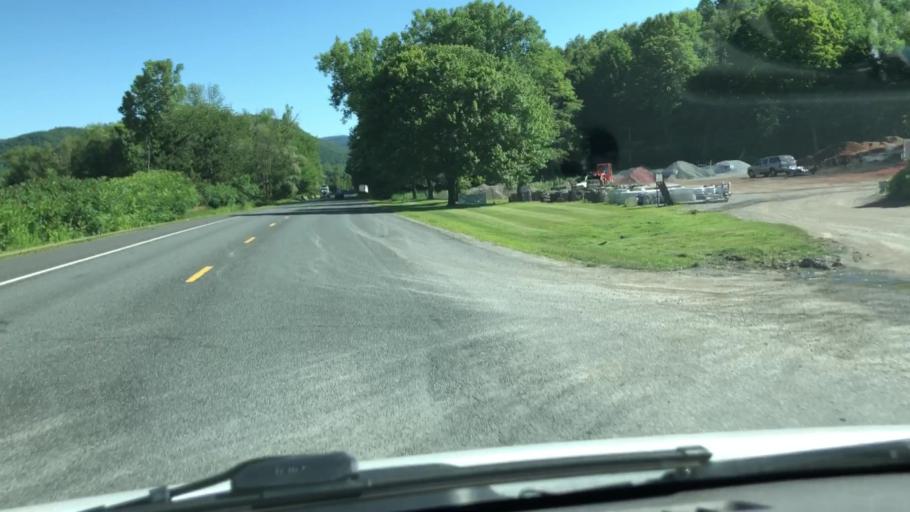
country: US
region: Massachusetts
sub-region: Berkshire County
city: Lanesborough
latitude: 42.5228
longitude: -73.1922
